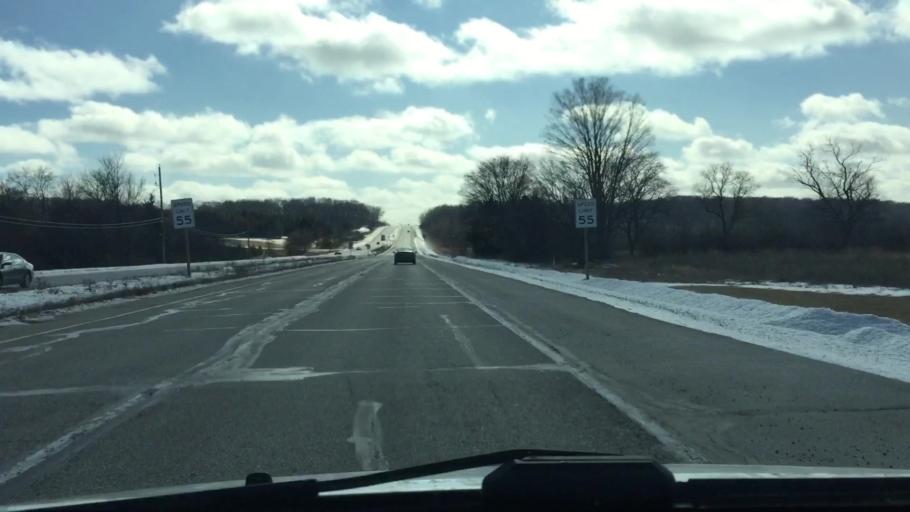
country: US
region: Wisconsin
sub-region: Waukesha County
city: Waukesha
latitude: 42.9464
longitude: -88.2283
